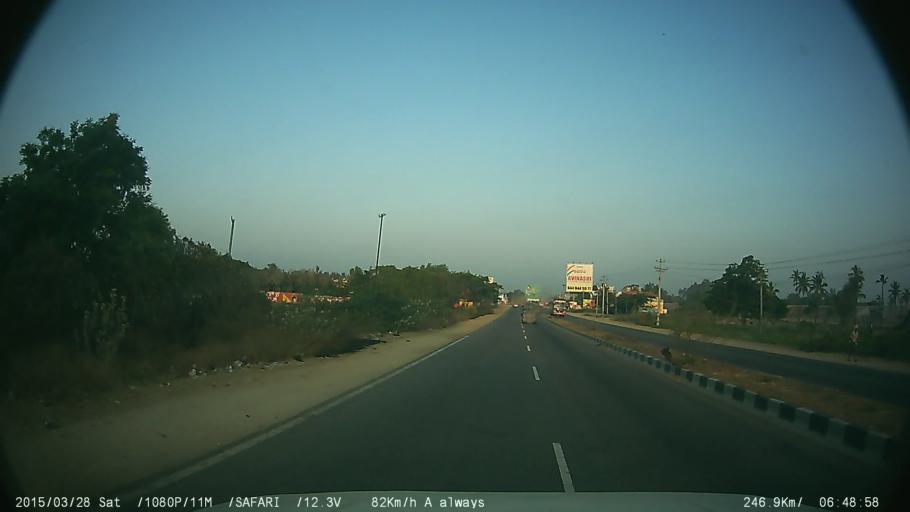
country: IN
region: Karnataka
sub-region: Mandya
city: Maddur
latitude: 12.6131
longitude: 77.0616
